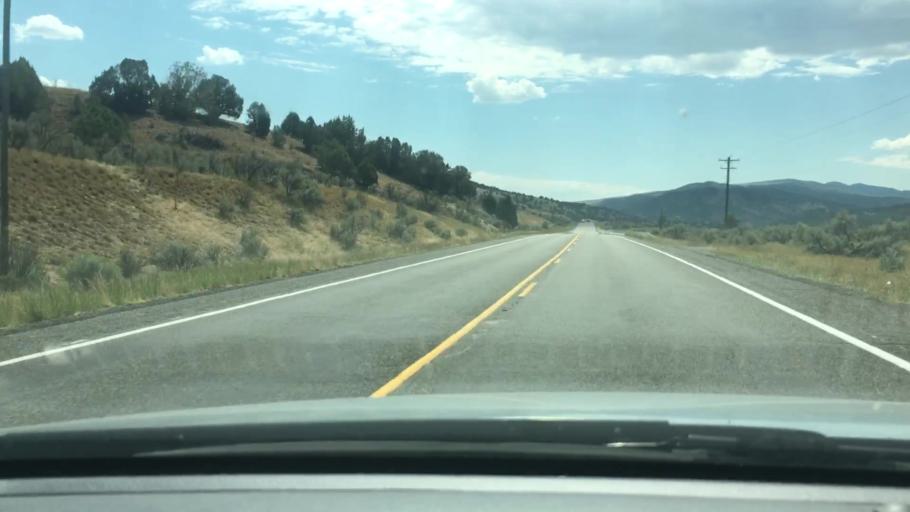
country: US
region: Utah
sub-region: Utah County
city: Woodland Hills
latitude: 39.9131
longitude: -111.5512
